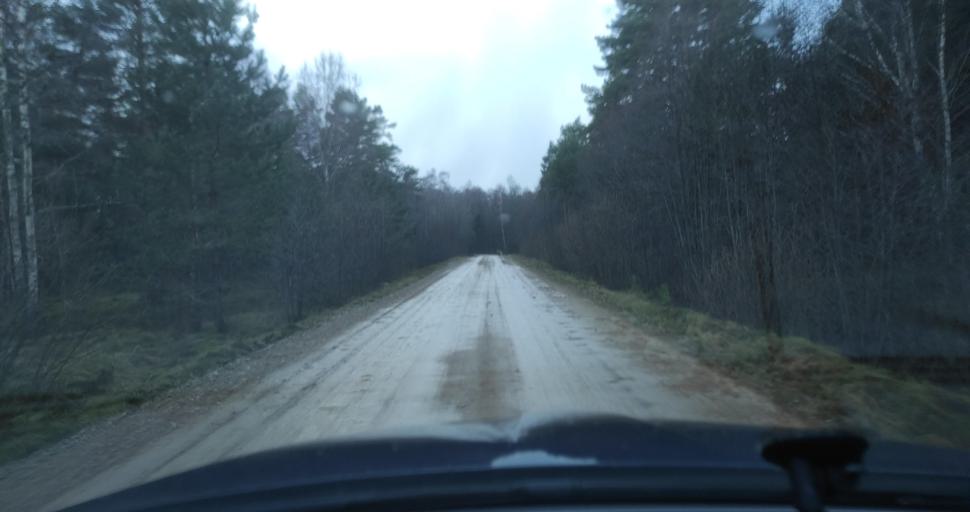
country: LV
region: Pavilostas
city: Pavilosta
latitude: 56.8429
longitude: 21.0880
